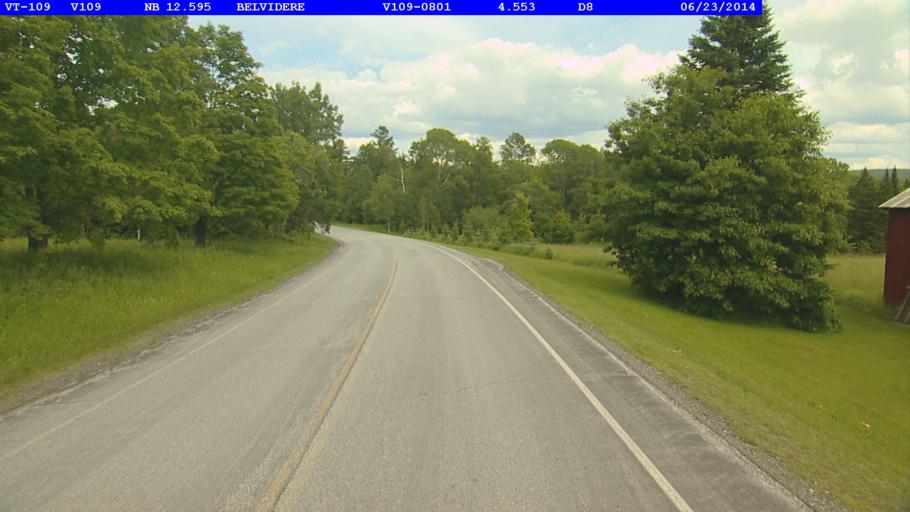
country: US
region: Vermont
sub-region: Lamoille County
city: Johnson
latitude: 44.7590
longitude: -72.6656
